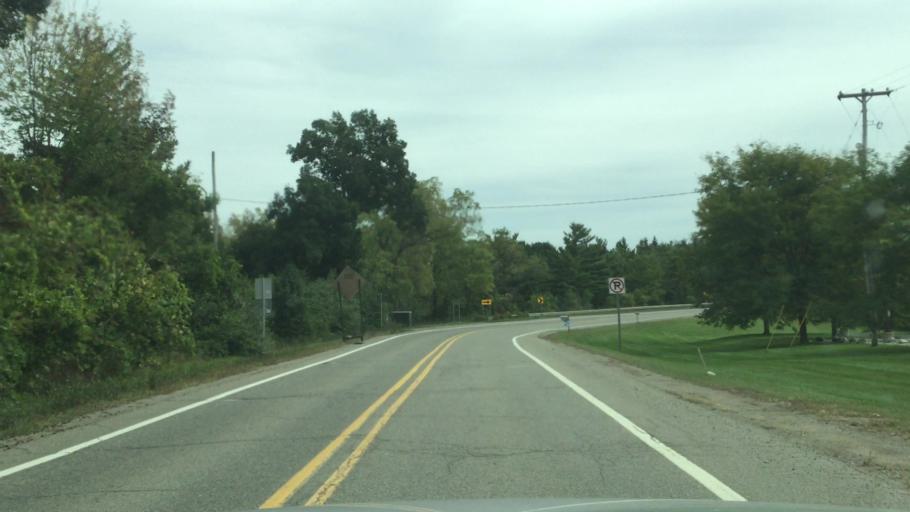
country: US
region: Michigan
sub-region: Oakland County
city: Holly
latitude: 42.8157
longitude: -83.5637
